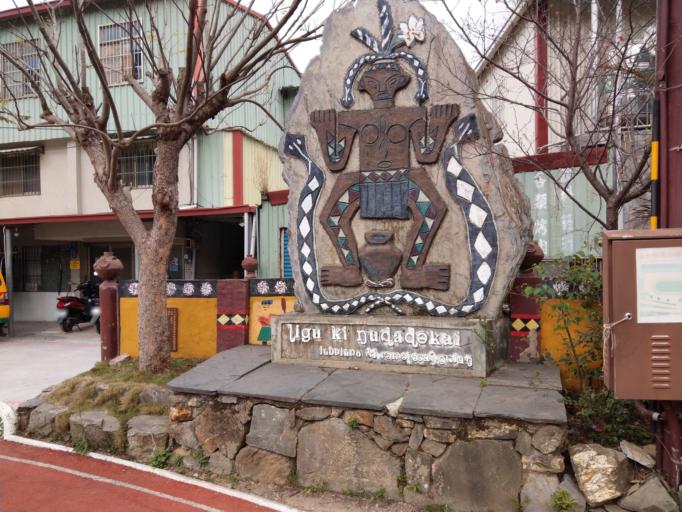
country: TW
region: Taiwan
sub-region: Pingtung
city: Pingtung
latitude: 22.7452
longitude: 120.7318
